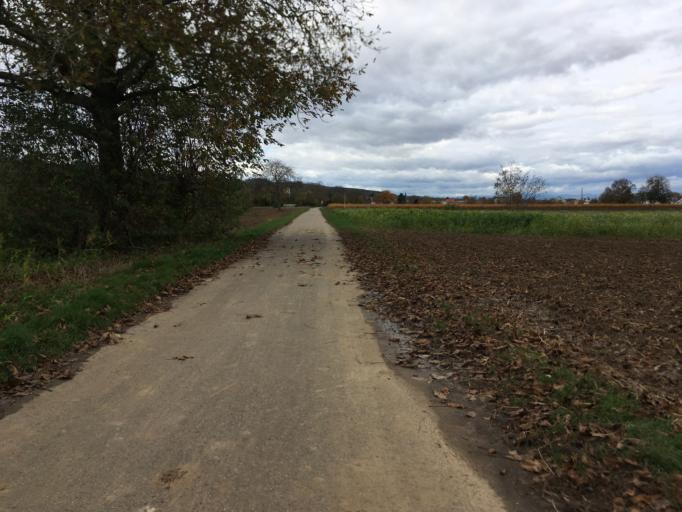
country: DE
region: Baden-Wuerttemberg
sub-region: Freiburg Region
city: Endingen
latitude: 48.1458
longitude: 7.7221
